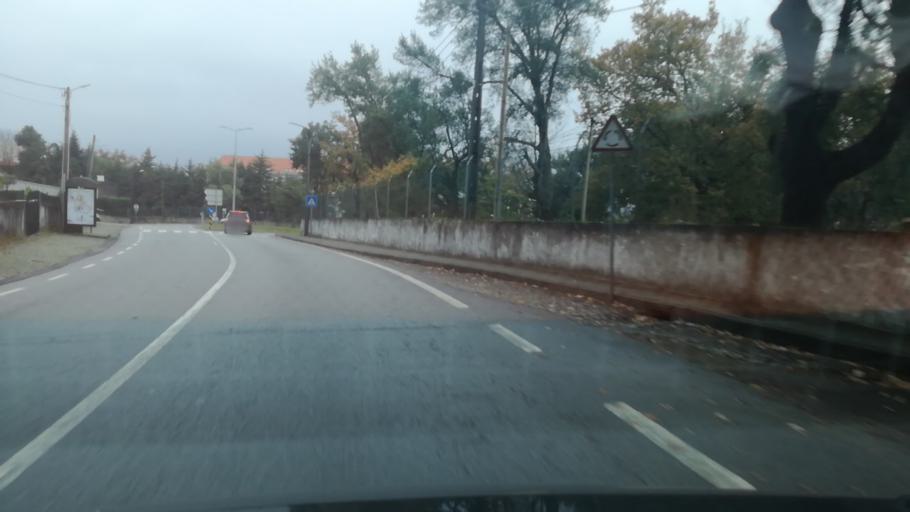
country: PT
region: Braga
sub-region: Braga
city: Braga
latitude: 41.5350
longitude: -8.4046
